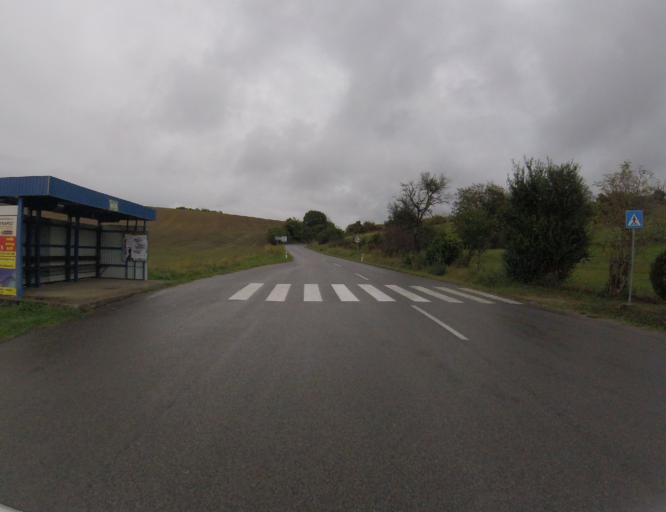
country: HU
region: Komarom-Esztergom
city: Esztergom
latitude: 47.8579
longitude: 18.7398
